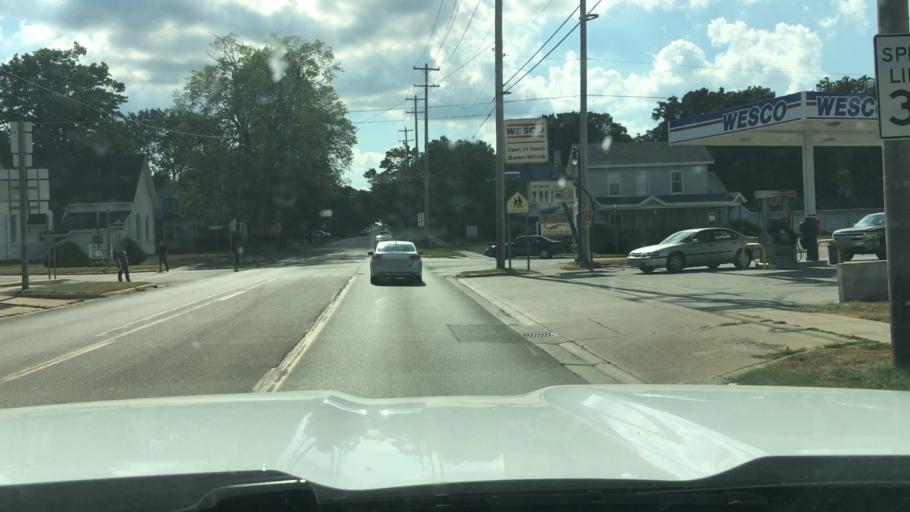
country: US
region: Michigan
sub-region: Montcalm County
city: Greenville
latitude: 43.1775
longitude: -85.2543
